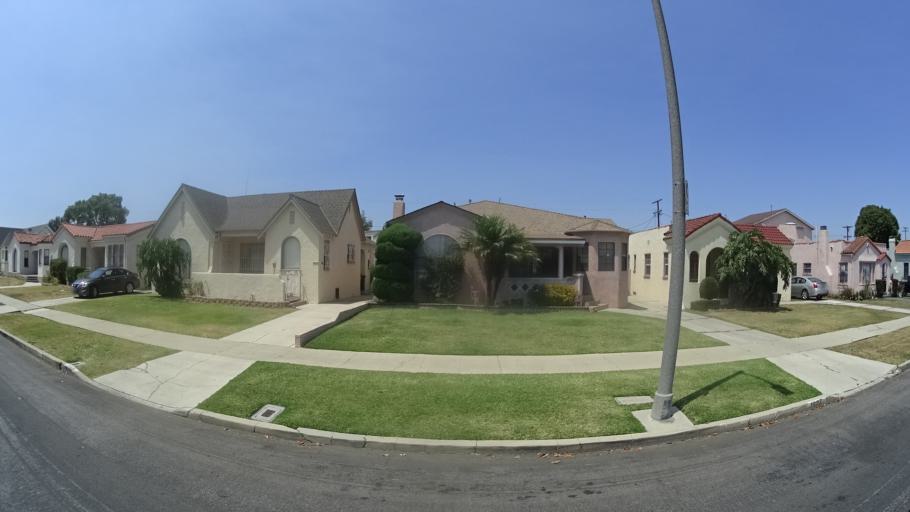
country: US
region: California
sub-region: Los Angeles County
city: Westmont
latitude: 33.9664
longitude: -118.3123
